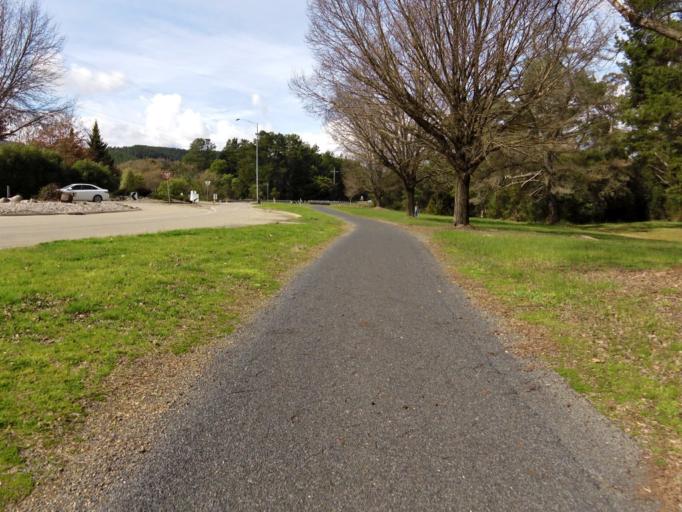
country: AU
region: Victoria
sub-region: Alpine
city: Mount Beauty
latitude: -36.7031
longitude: 146.9235
